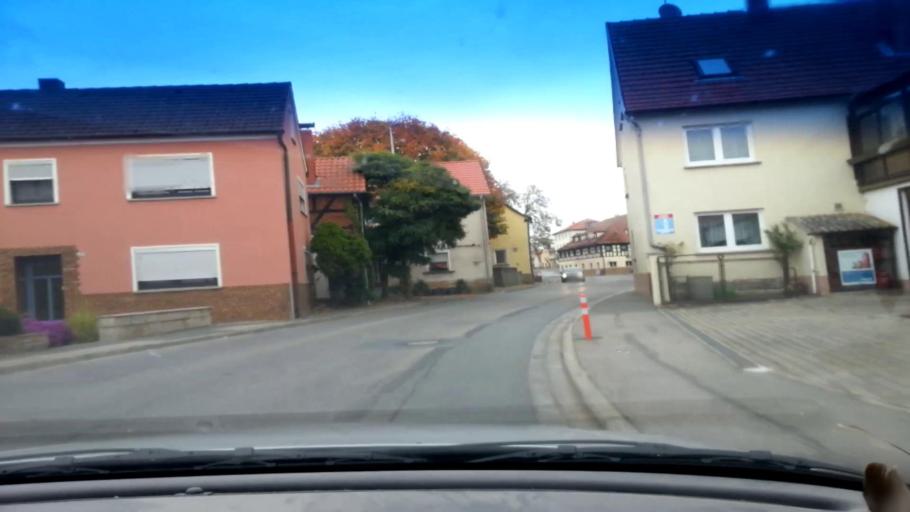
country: DE
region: Bavaria
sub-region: Upper Franconia
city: Reckendorf
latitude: 50.0188
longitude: 10.8267
